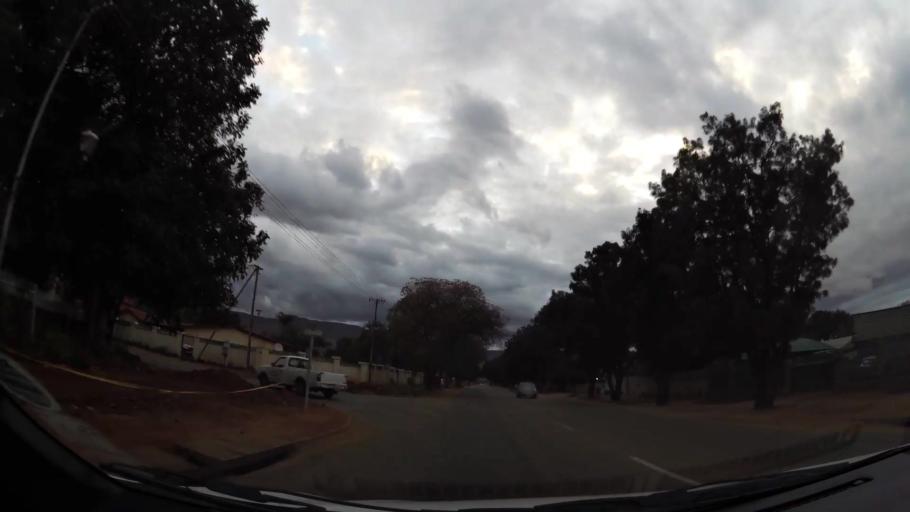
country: ZA
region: Limpopo
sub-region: Waterberg District Municipality
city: Mokopane
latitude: -24.1890
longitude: 28.9925
